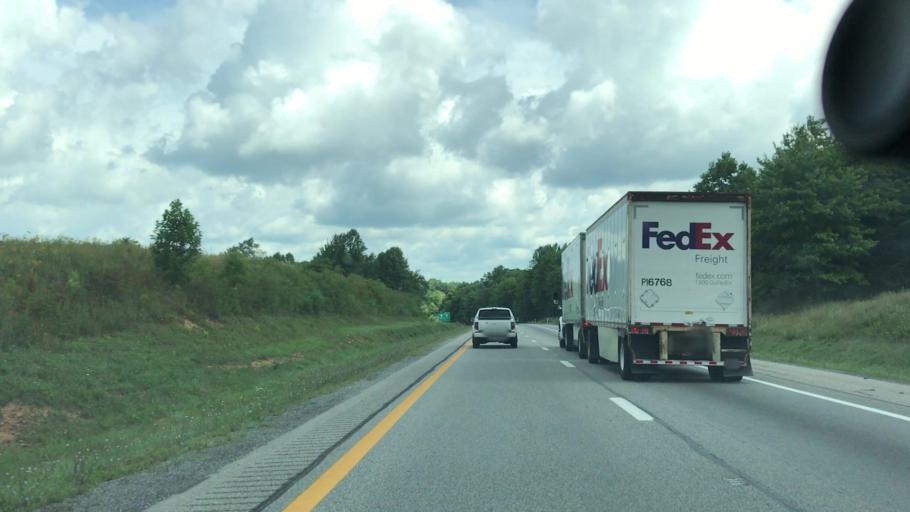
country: US
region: West Virginia
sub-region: Mercer County
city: Athens
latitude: 37.4031
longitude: -81.0613
